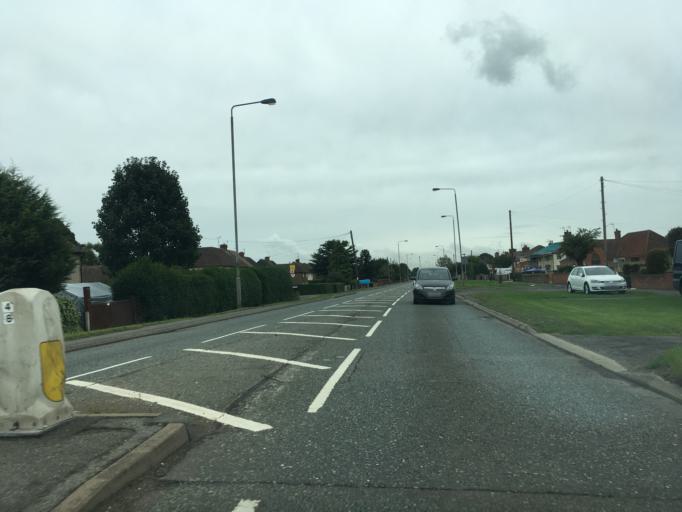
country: GB
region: England
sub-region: Nottinghamshire
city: Newark on Trent
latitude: 53.0893
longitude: -0.7930
